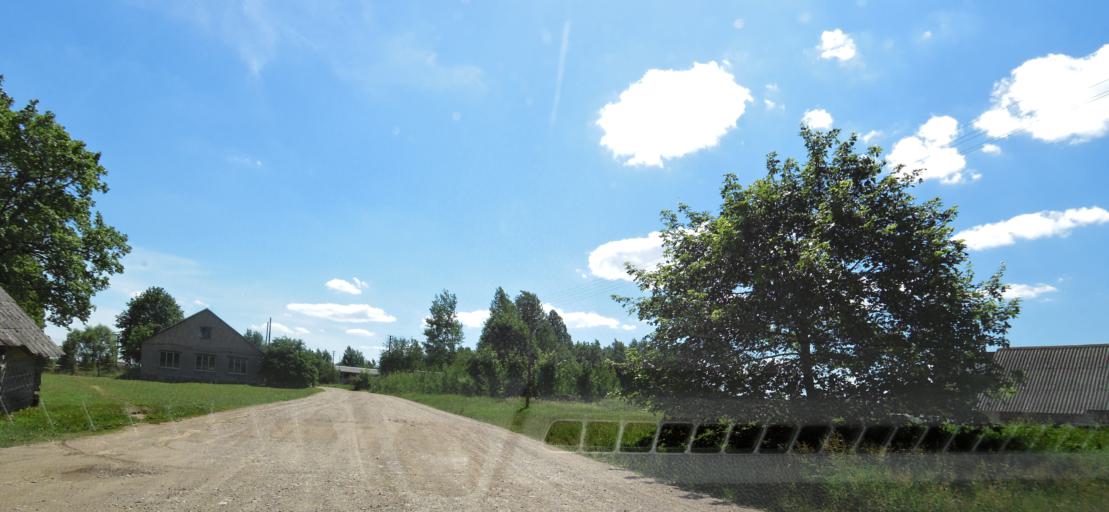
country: LT
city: Nemencine
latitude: 54.8720
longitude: 25.3609
